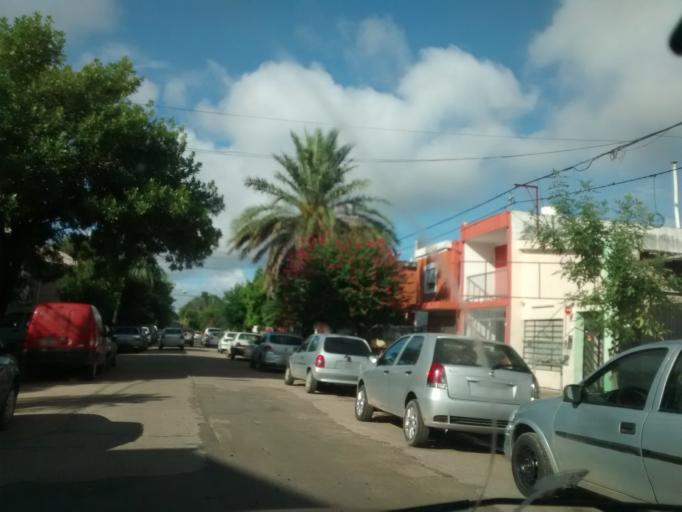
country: AR
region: Chaco
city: Resistencia
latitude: -27.4545
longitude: -58.9920
